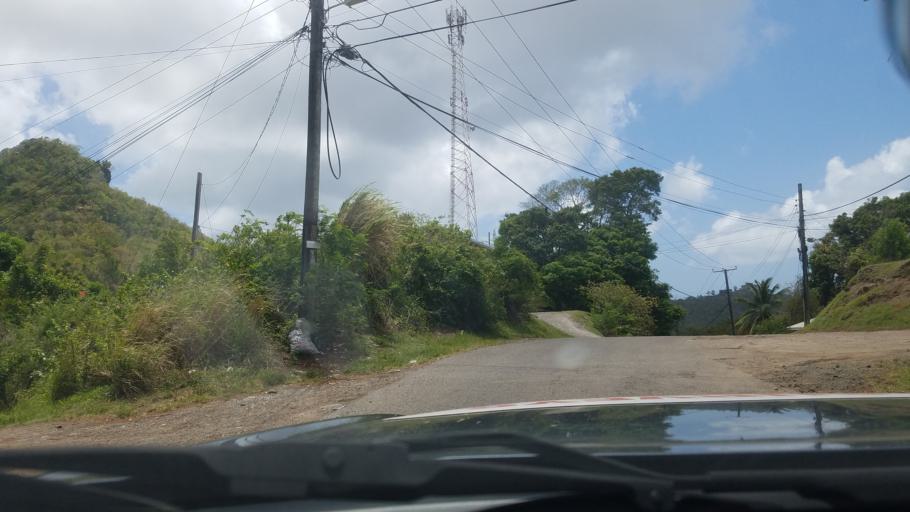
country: LC
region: Gros-Islet
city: Gros Islet
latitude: 14.0573
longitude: -60.9379
